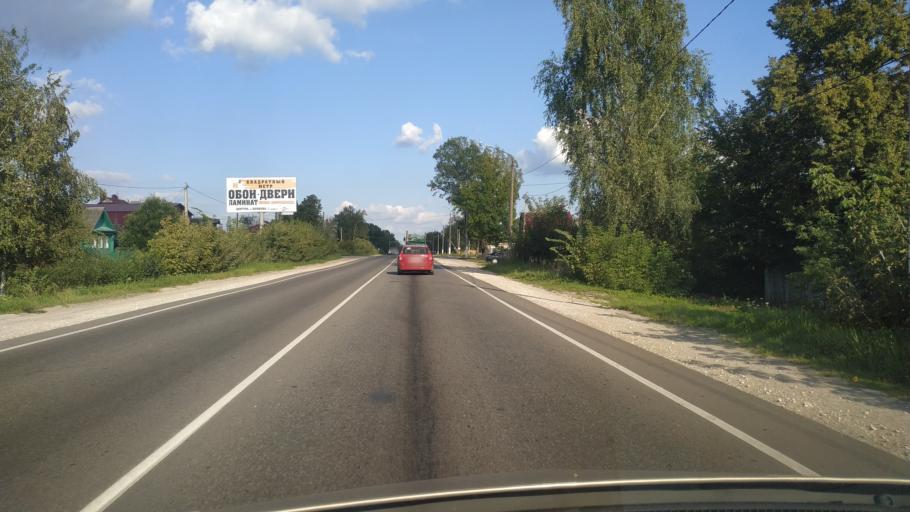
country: RU
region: Moskovskaya
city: Shaturtorf
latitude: 55.5795
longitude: 39.4734
